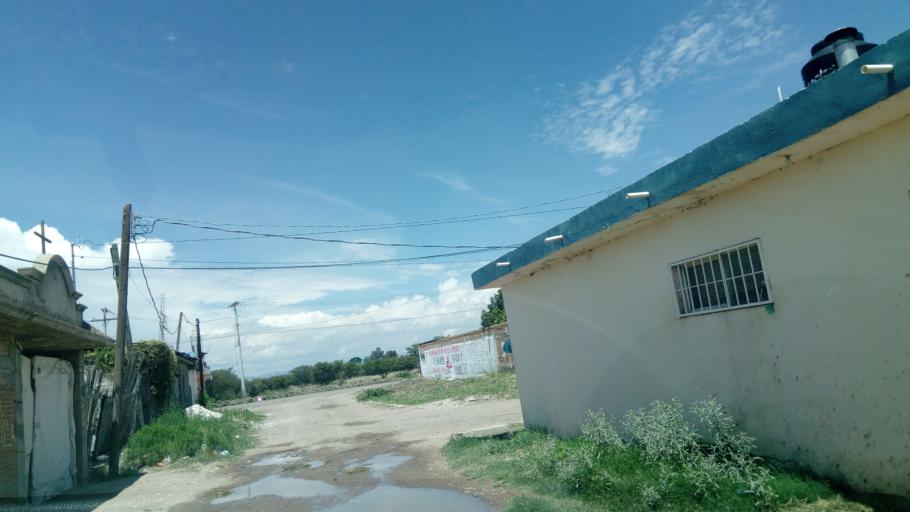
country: MX
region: Durango
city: Victoria de Durango
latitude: 24.0213
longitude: -104.5949
